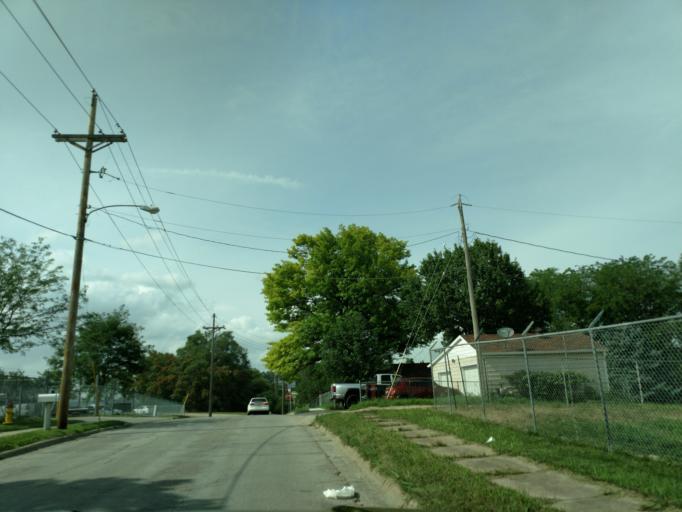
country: US
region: Nebraska
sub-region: Douglas County
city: Omaha
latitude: 41.1957
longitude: -95.9456
